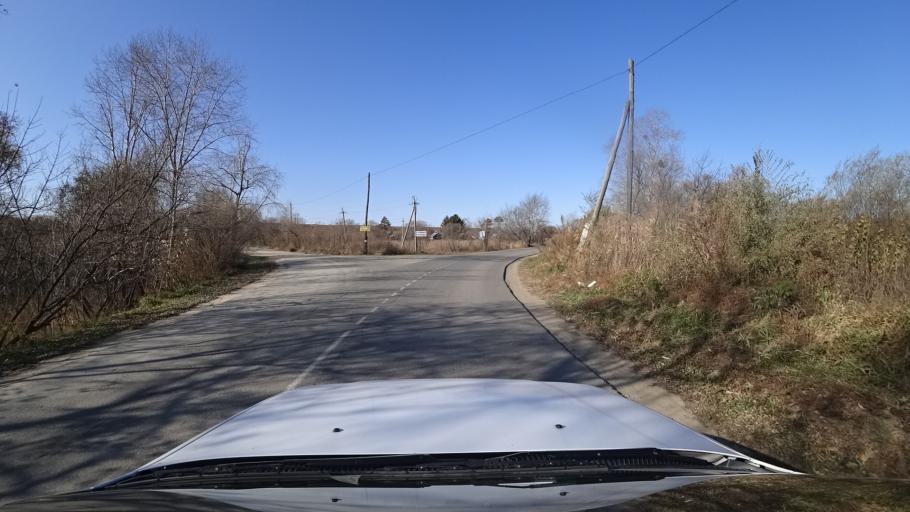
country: RU
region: Primorskiy
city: Dal'nerechensk
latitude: 45.9331
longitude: 133.7130
